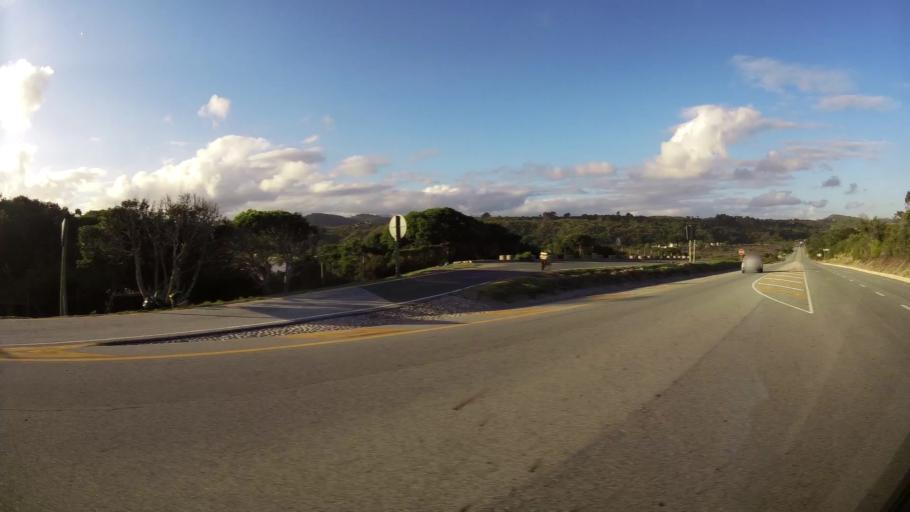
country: ZA
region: Western Cape
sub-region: Eden District Municipality
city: George
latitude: -34.0011
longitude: 22.6466
